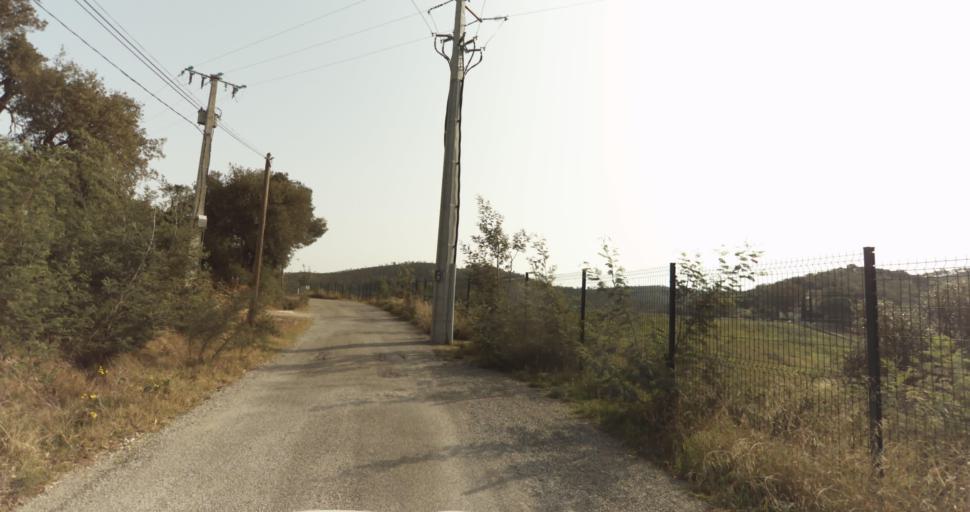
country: FR
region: Provence-Alpes-Cote d'Azur
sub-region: Departement du Var
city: Bormes-les-Mimosas
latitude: 43.1416
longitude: 6.2903
